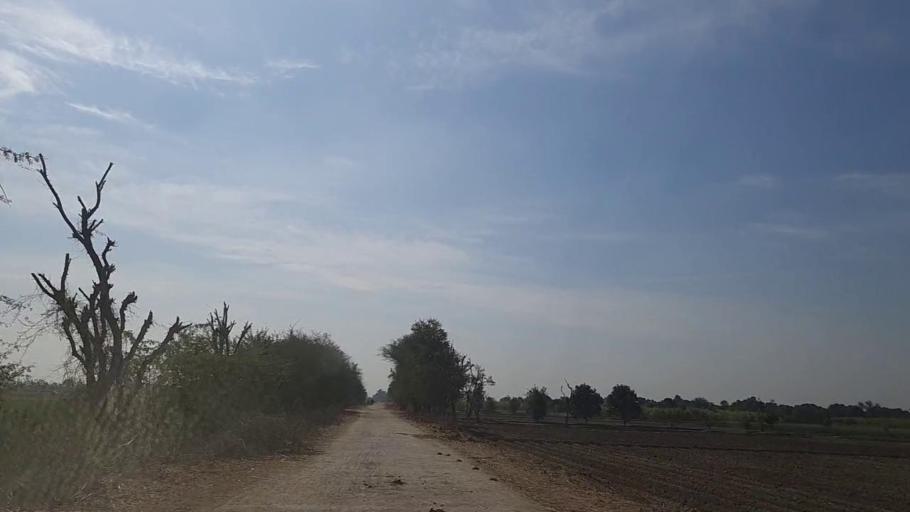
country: PK
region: Sindh
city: Mirpur Khas
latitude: 25.4761
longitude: 68.9640
